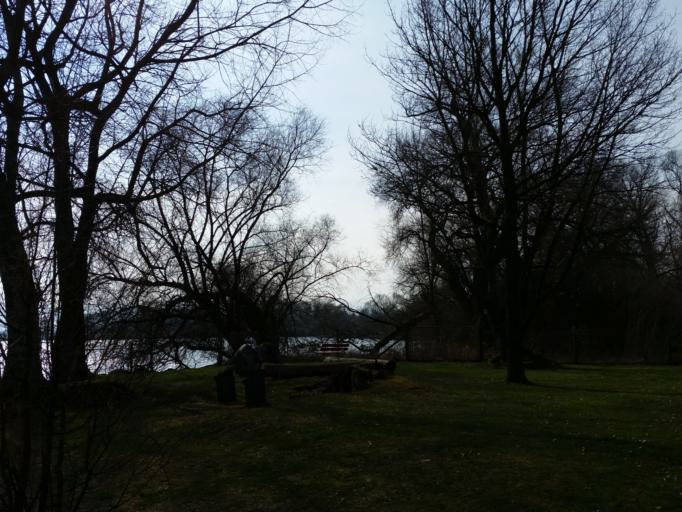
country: CH
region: Thurgau
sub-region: Arbon District
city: Romanshorn
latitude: 47.5554
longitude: 9.3804
